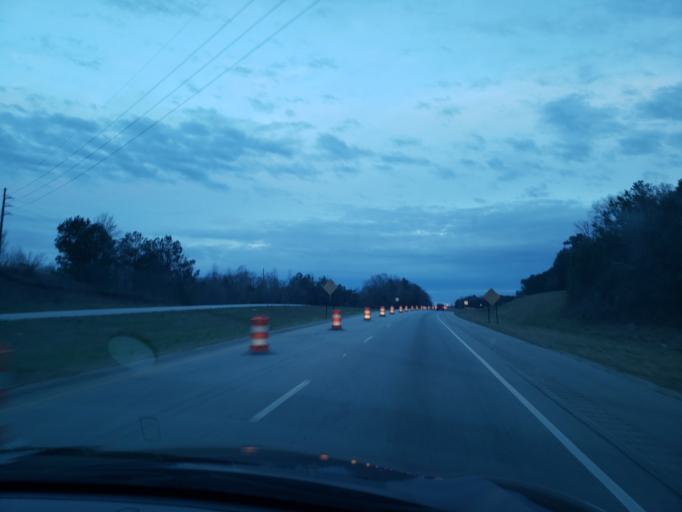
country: US
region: Alabama
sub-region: Lee County
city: Auburn
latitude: 32.6687
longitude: -85.4783
